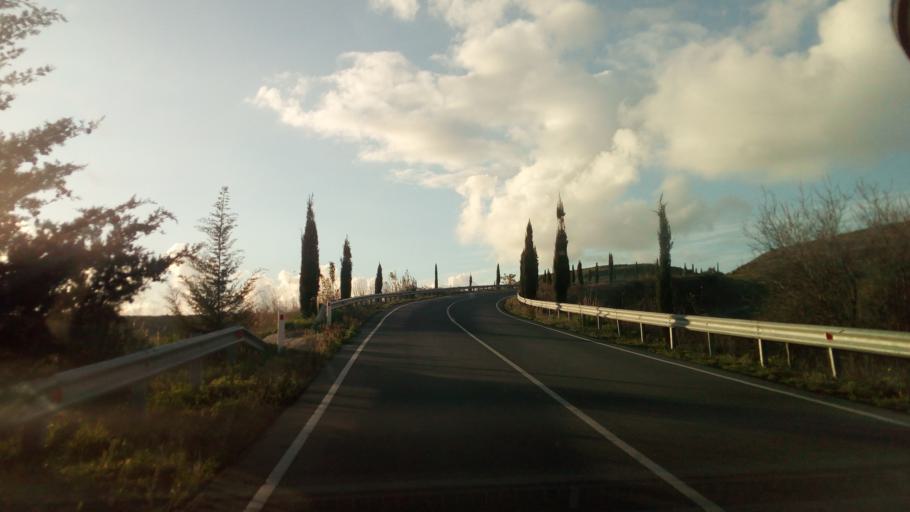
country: CY
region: Pafos
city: Mesogi
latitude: 34.9134
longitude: 32.5452
